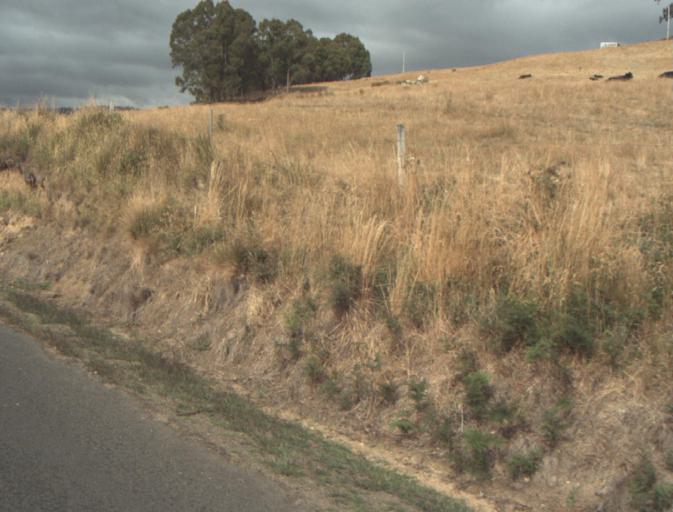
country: AU
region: Tasmania
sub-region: Dorset
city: Scottsdale
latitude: -41.4597
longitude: 147.5960
